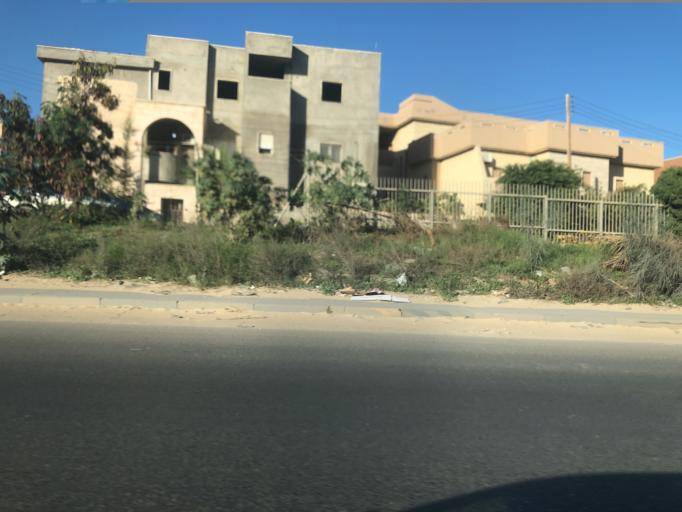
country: LY
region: Tripoli
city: Tagiura
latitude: 32.8698
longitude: 13.2719
